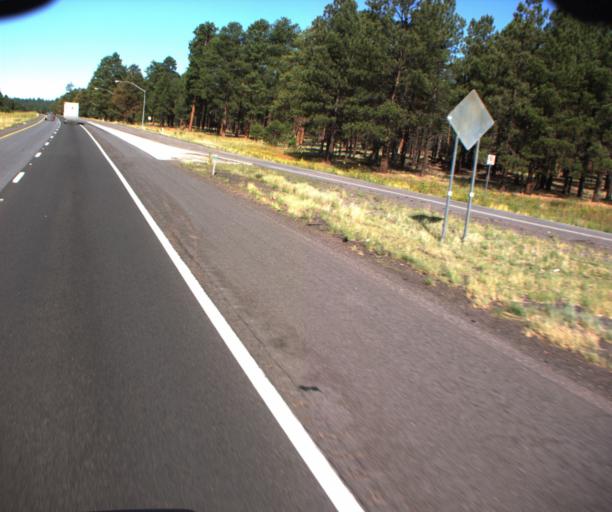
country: US
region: Arizona
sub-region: Coconino County
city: Parks
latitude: 35.2492
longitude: -111.8705
